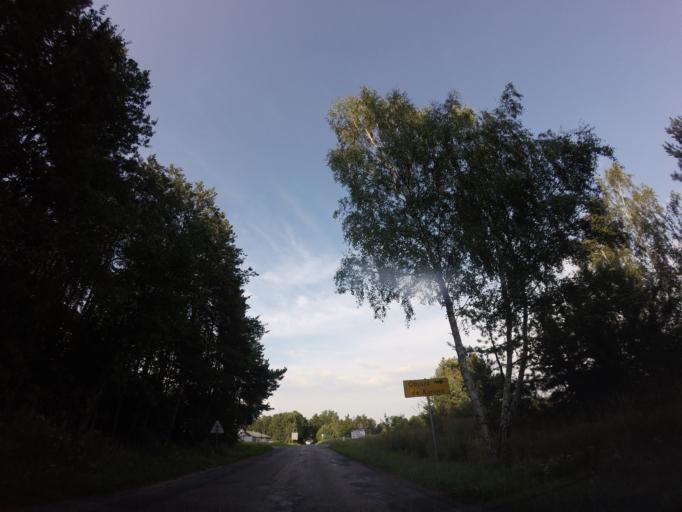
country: PL
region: Lublin Voivodeship
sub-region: Powiat pulawski
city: Kurow
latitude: 51.4303
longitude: 22.2152
